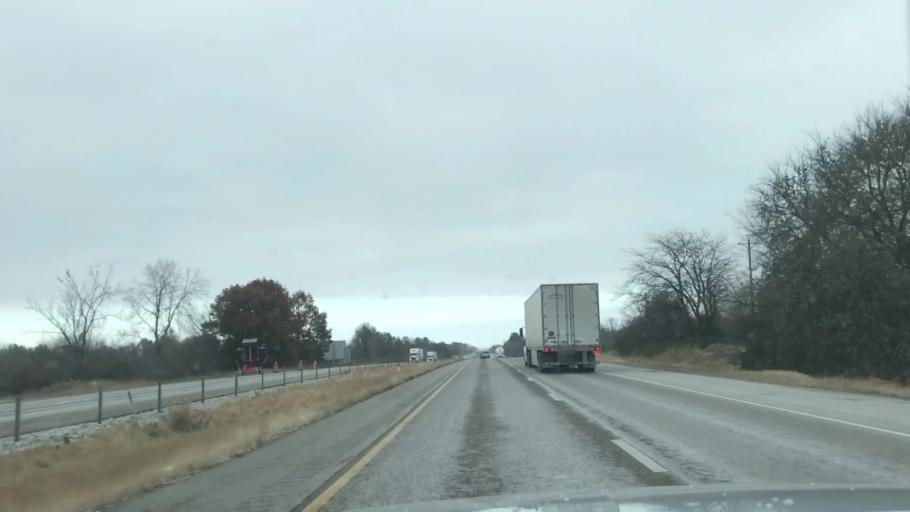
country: US
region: Illinois
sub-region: Madison County
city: Troy
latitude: 38.7598
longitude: -89.9050
